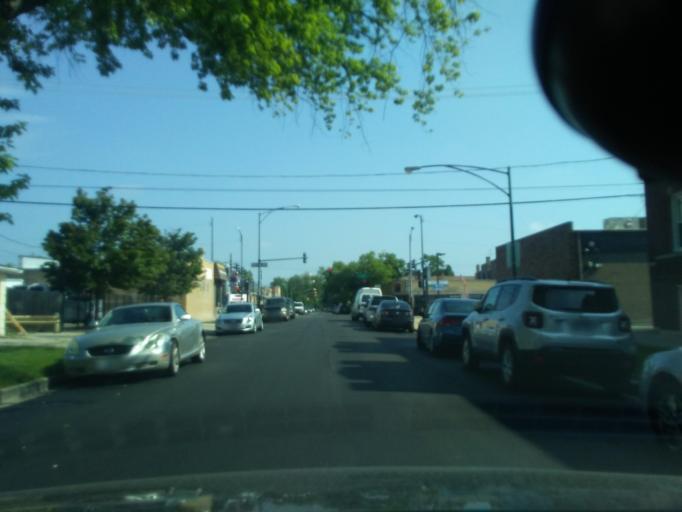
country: US
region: Illinois
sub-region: Cook County
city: Elmwood Park
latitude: 41.9307
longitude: -87.7613
